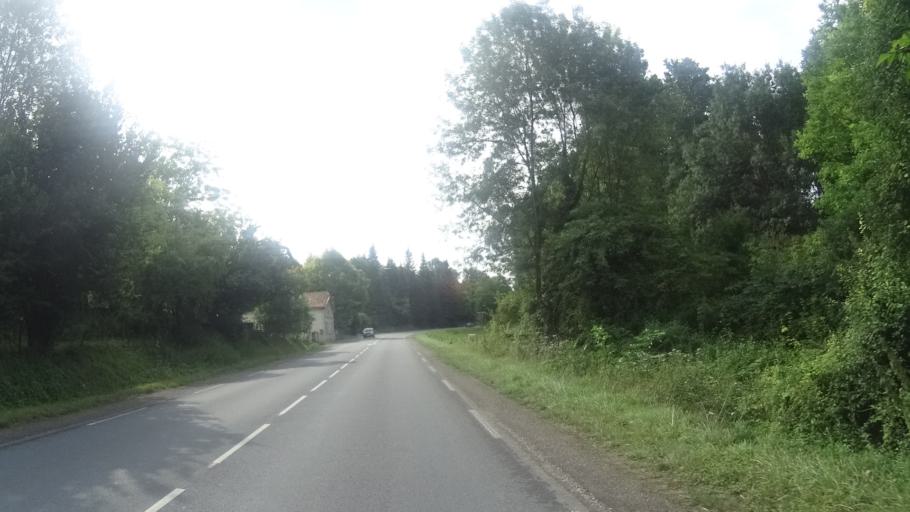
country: FR
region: Aquitaine
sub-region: Departement de la Dordogne
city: Riberac
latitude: 45.2332
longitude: 0.3553
